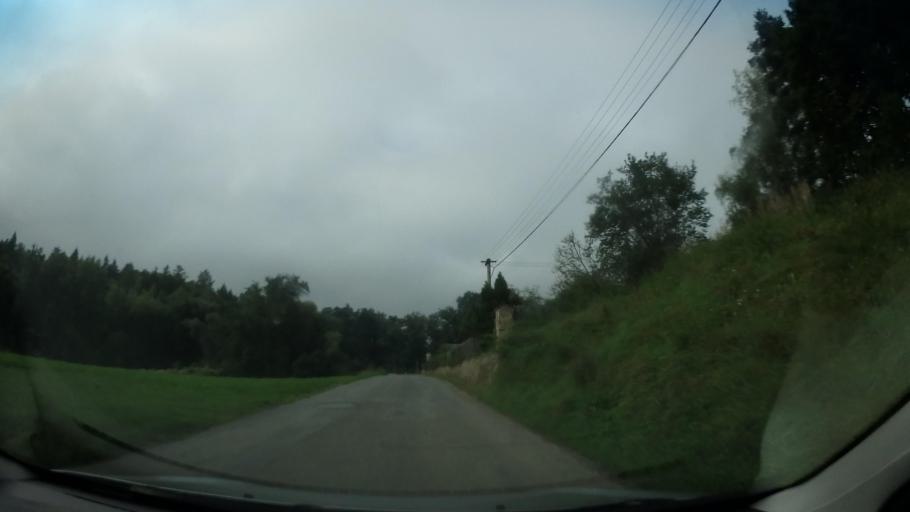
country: CZ
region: Central Bohemia
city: Sedlcany
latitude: 49.7143
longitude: 14.4106
